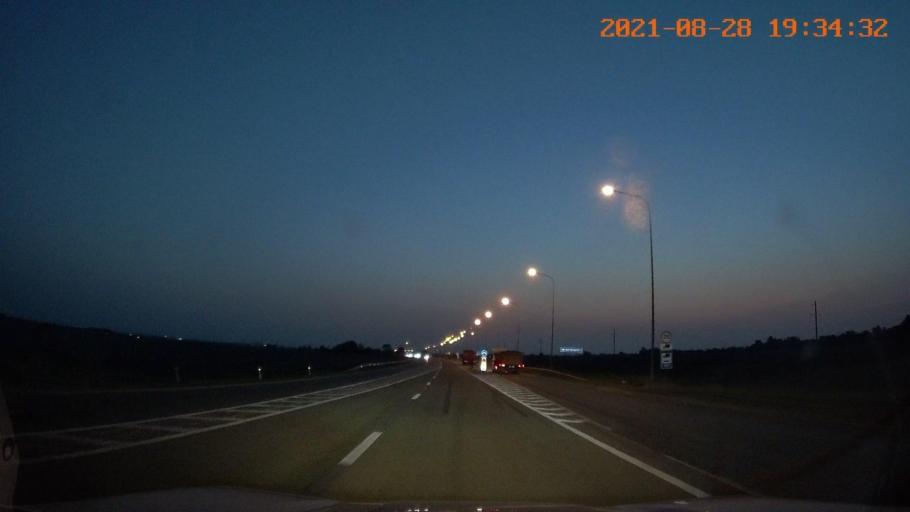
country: RU
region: Adygeya
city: Adygeysk
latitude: 44.9162
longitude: 39.2797
